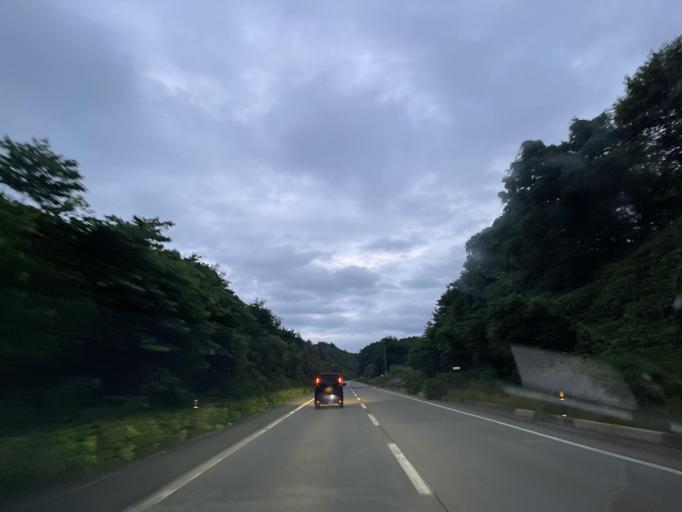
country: JP
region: Iwate
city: Morioka-shi
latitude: 39.8457
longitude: 141.1741
